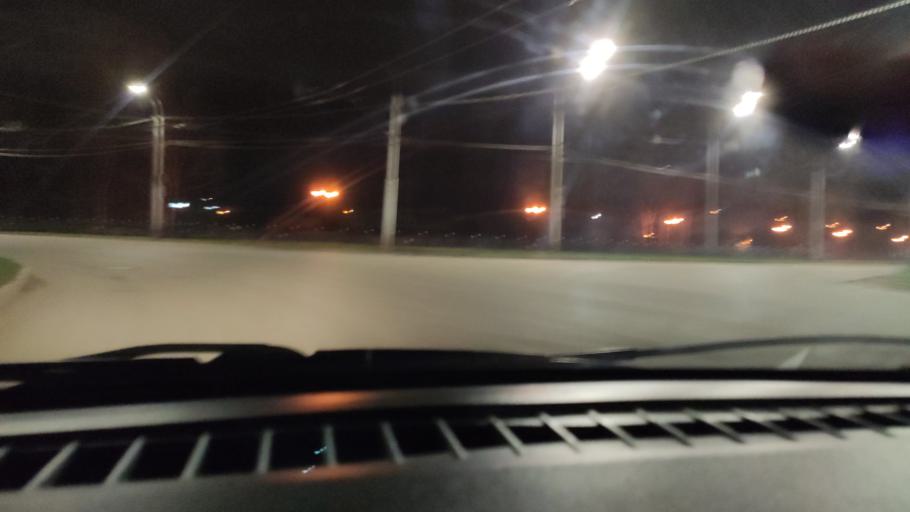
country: RU
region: Bashkortostan
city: Sterlitamak
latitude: 53.6373
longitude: 55.9105
